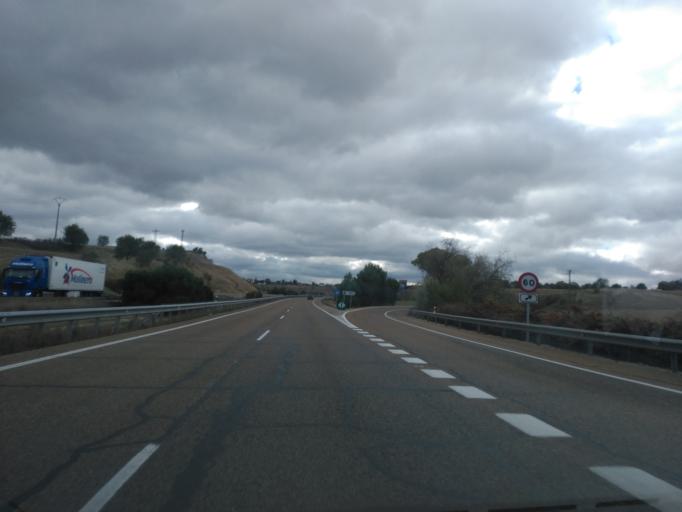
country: ES
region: Castille and Leon
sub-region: Provincia de Valladolid
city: Valladolid
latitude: 41.6879
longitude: -4.7278
